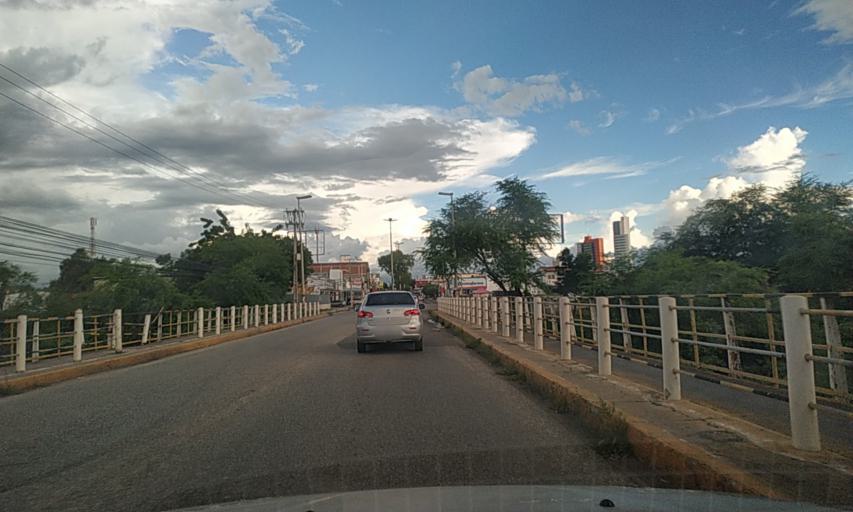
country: BR
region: Rio Grande do Norte
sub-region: Mossoro
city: Mossoro
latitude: -5.2032
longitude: -37.3375
